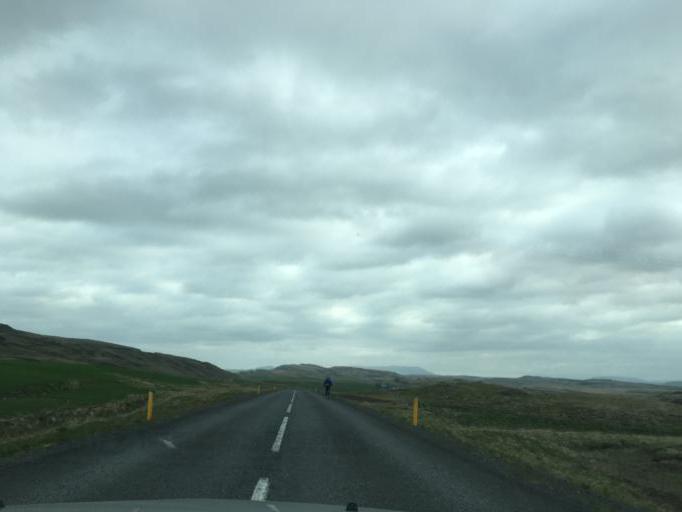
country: IS
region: South
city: Vestmannaeyjar
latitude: 64.2288
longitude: -20.2480
